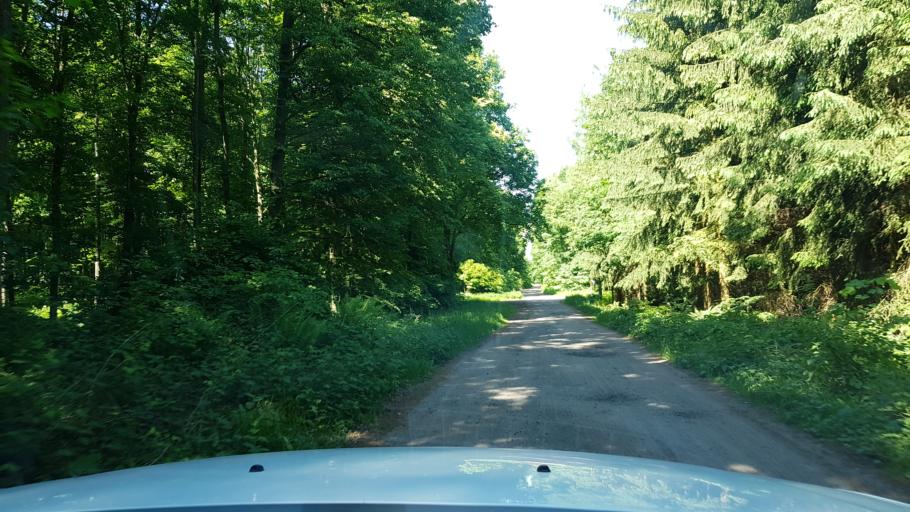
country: PL
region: West Pomeranian Voivodeship
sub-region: Powiat gryfinski
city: Banie
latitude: 53.1149
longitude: 14.5400
